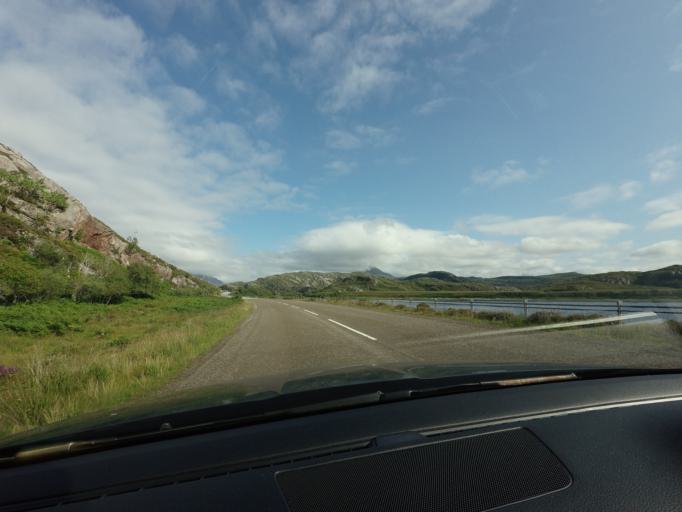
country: GB
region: Scotland
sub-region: Highland
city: Ullapool
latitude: 58.3801
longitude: -5.0303
